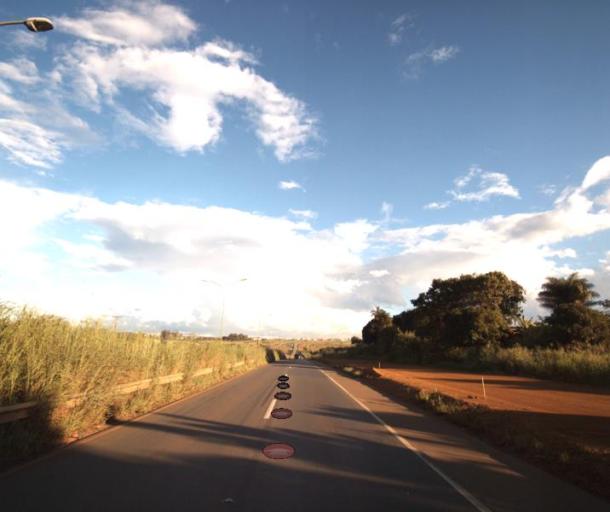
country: BR
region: Goias
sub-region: Anapolis
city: Anapolis
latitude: -16.3030
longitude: -48.9253
